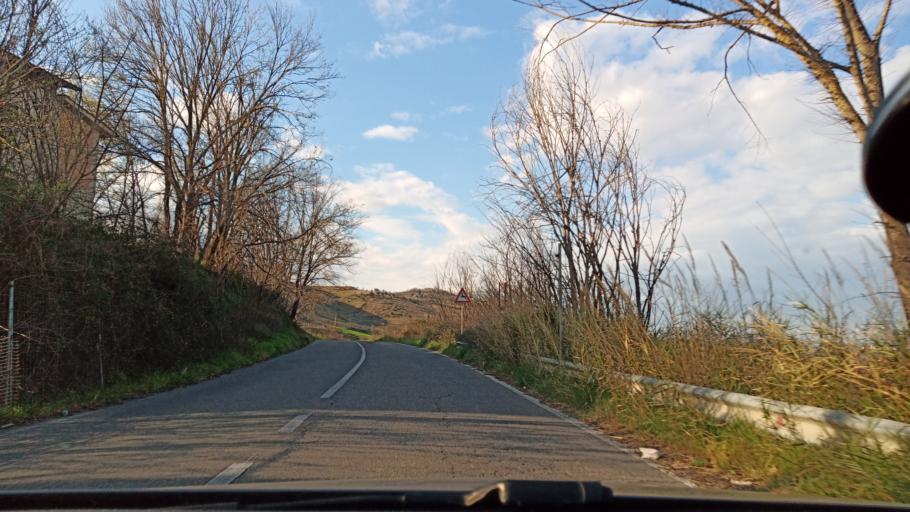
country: IT
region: Latium
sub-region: Citta metropolitana di Roma Capitale
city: Civitella San Paolo
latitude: 42.1868
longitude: 12.6044
